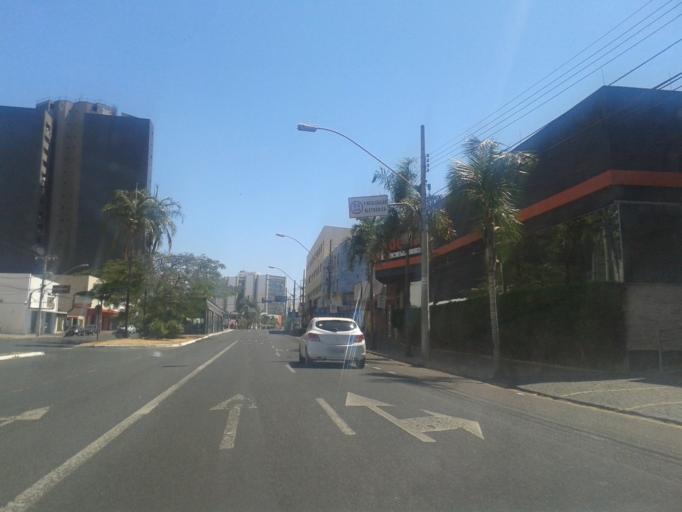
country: BR
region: Minas Gerais
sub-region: Uberlandia
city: Uberlandia
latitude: -18.9162
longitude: -48.2709
